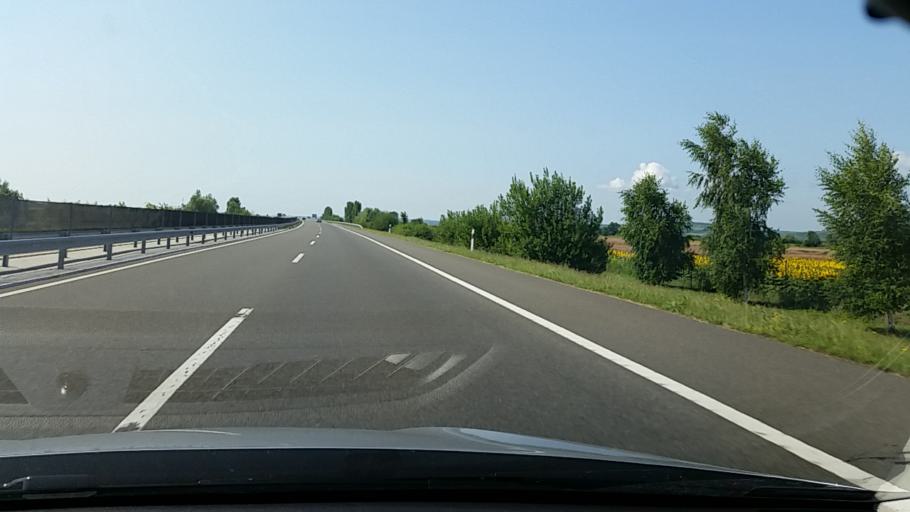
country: HU
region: Tolna
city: Ocseny
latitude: 46.2970
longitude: 18.7203
